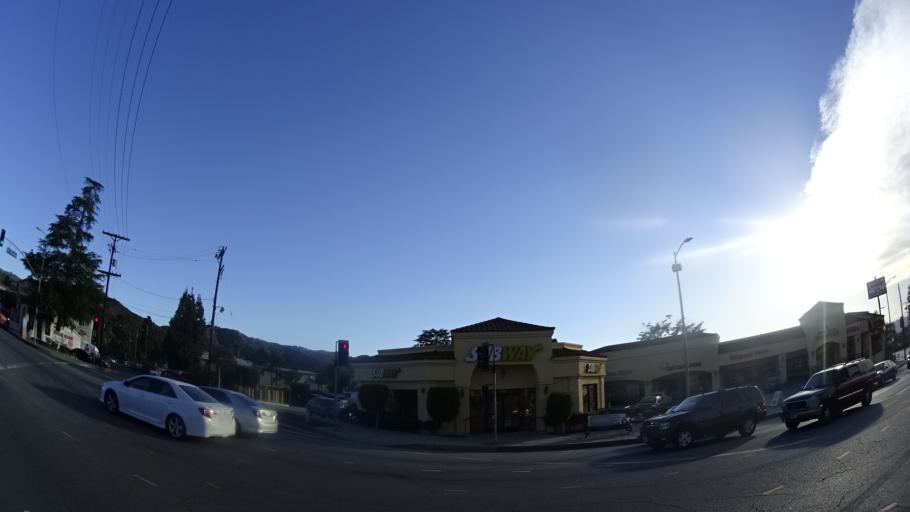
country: US
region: California
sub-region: Los Angeles County
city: La Crescenta-Montrose
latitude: 34.2591
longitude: -118.3025
